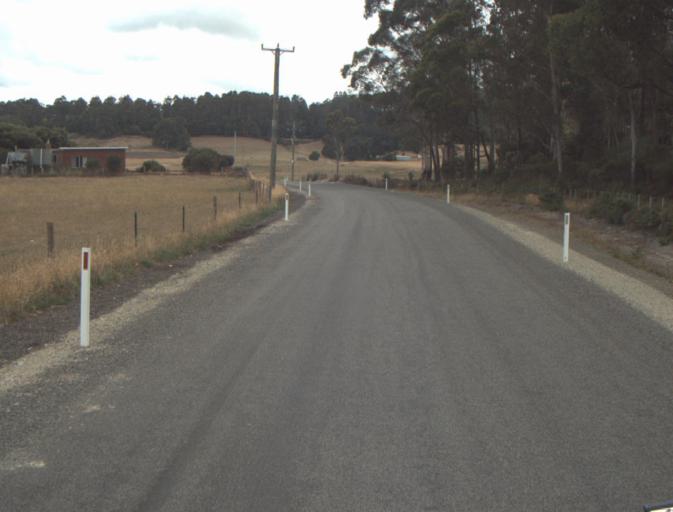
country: AU
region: Tasmania
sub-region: Launceston
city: Mayfield
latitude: -41.2078
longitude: 147.1878
